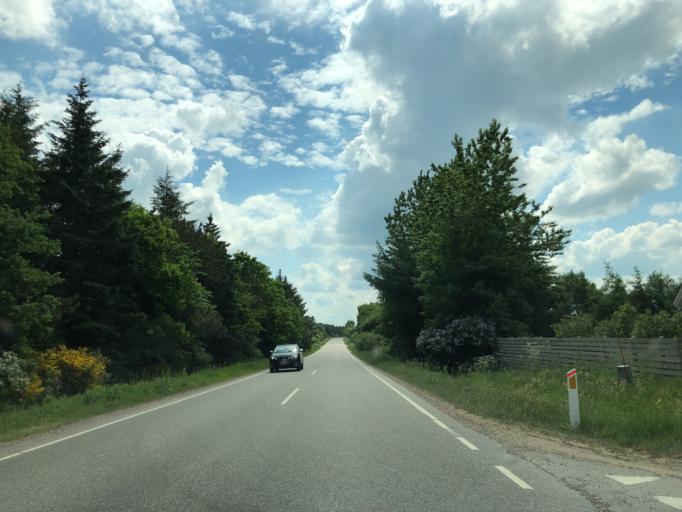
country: DK
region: Central Jutland
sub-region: Holstebro Kommune
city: Ulfborg
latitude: 56.3698
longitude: 8.3331
